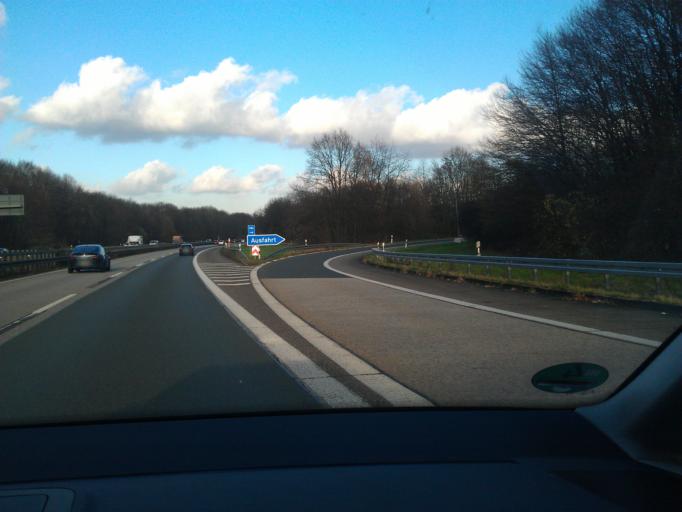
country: DE
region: North Rhine-Westphalia
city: Sprockhovel
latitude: 51.4146
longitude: 7.2620
